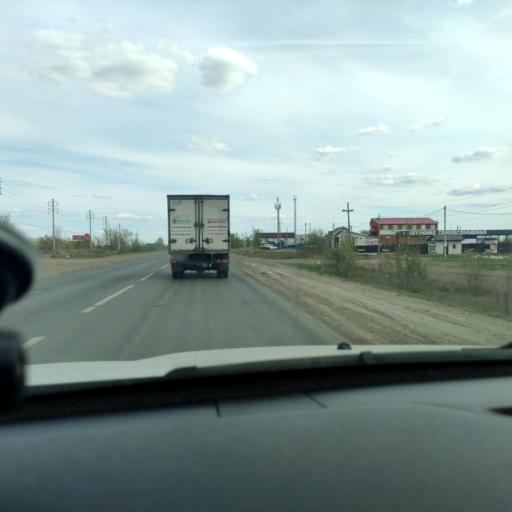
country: RU
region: Samara
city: Kinel'
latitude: 53.2131
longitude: 50.6159
